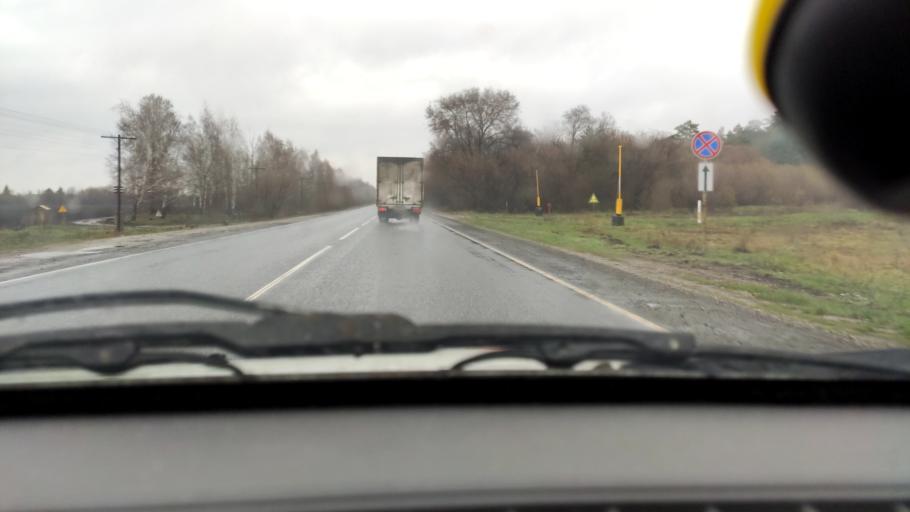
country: RU
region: Samara
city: Povolzhskiy
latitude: 53.6040
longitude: 49.6022
